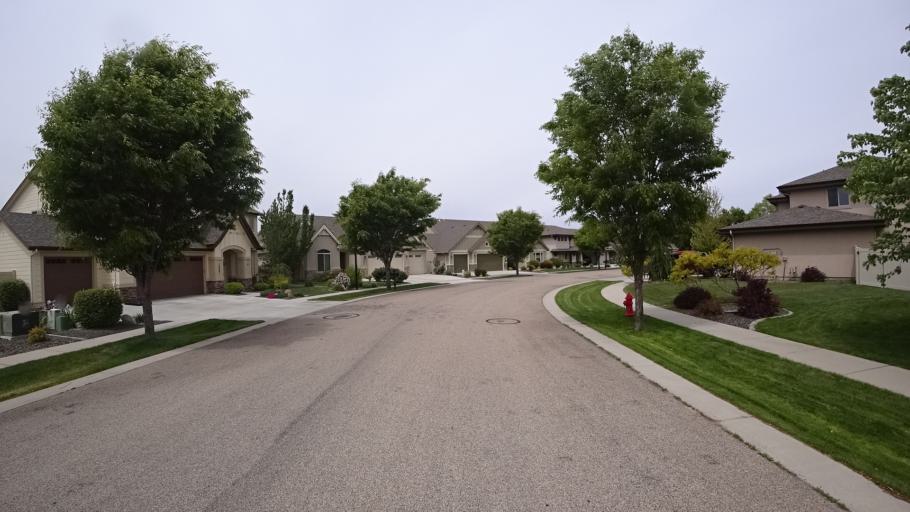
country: US
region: Idaho
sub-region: Ada County
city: Meridian
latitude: 43.5651
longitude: -116.3630
